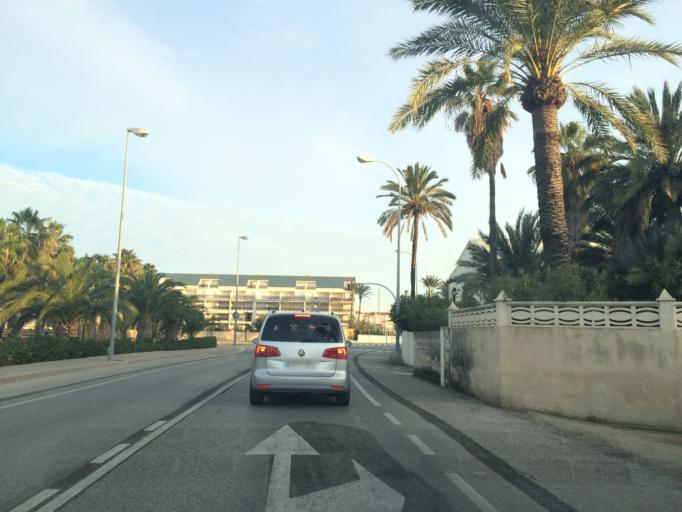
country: ES
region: Valencia
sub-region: Provincia de Alicante
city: Denia
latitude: 38.8522
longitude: 0.0920
